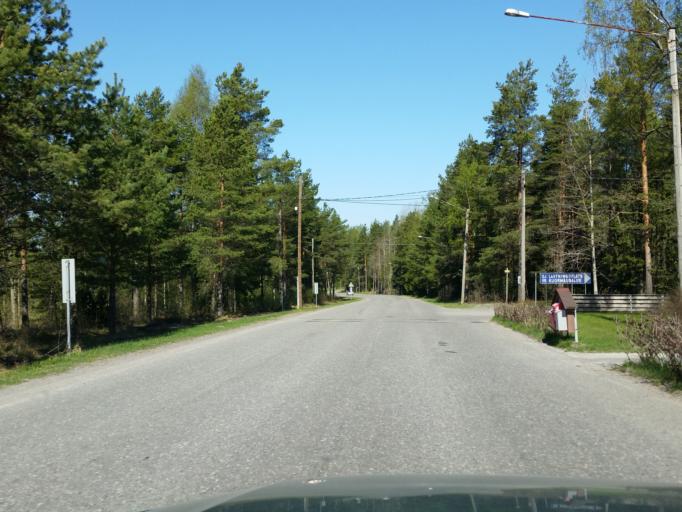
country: FI
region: Uusimaa
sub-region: Raaseporin
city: Inga
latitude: 60.1386
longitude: 23.8618
